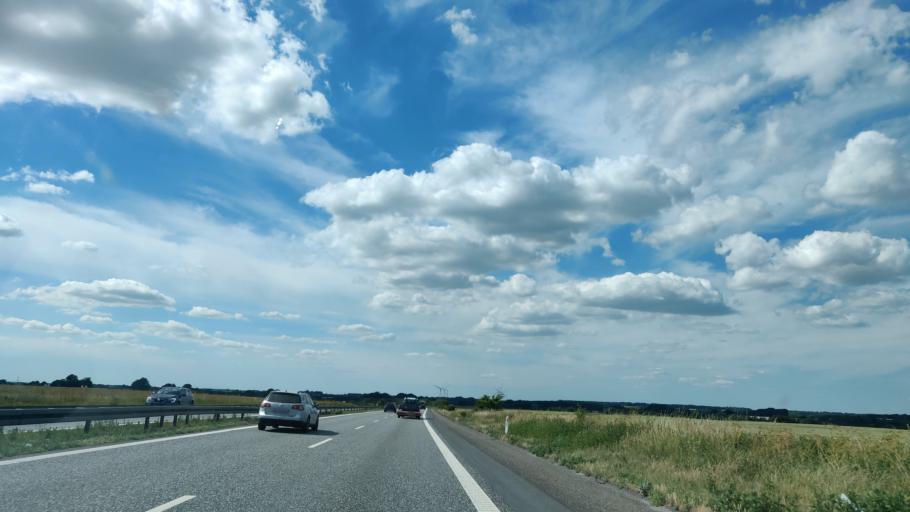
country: DK
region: Central Jutland
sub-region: Randers Kommune
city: Spentrup
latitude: 56.5317
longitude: 9.9299
